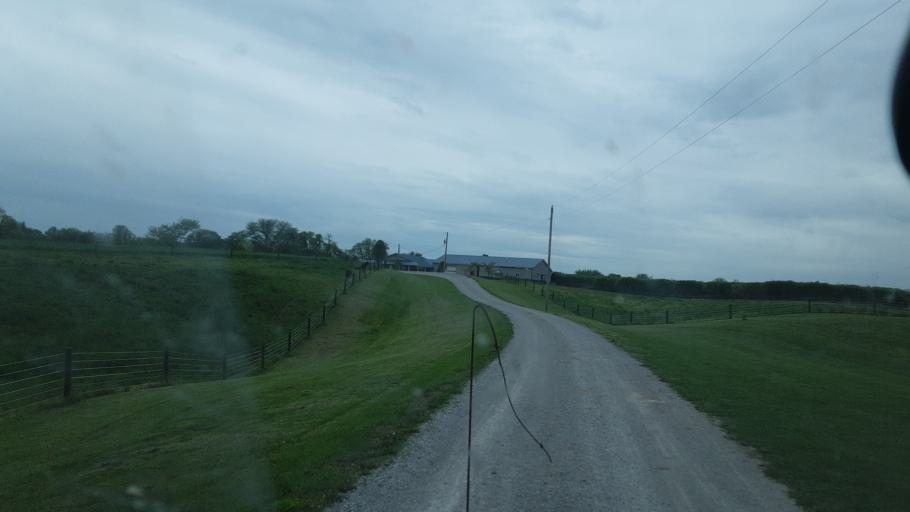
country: US
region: Illinois
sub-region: Jackson County
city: Murphysboro
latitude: 37.6794
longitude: -89.3076
